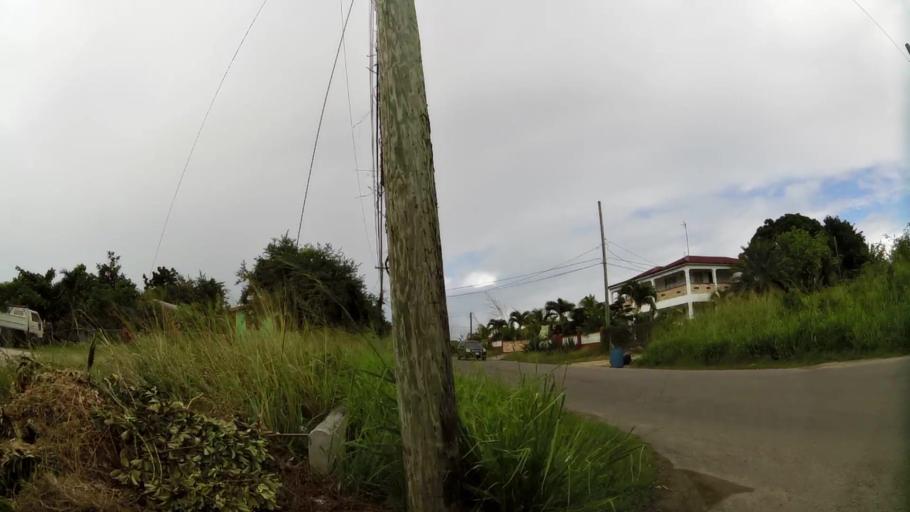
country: AG
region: Saint John
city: Potters Village
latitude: 17.0935
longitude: -61.8138
